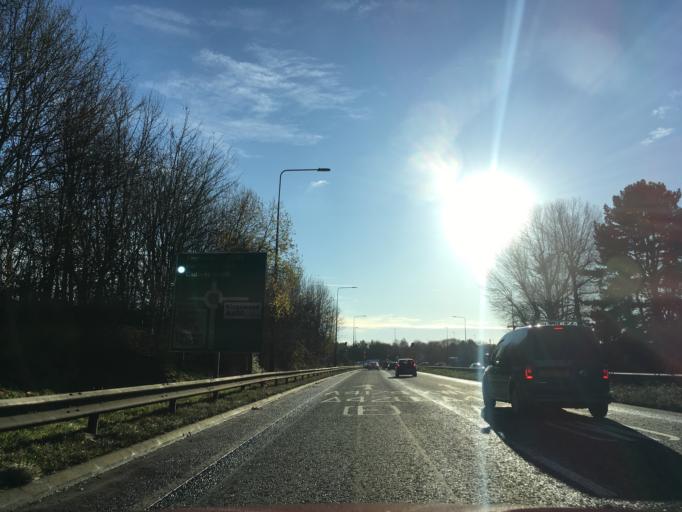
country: GB
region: England
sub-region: South Gloucestershire
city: Kingswood
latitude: 51.4622
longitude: -2.4821
